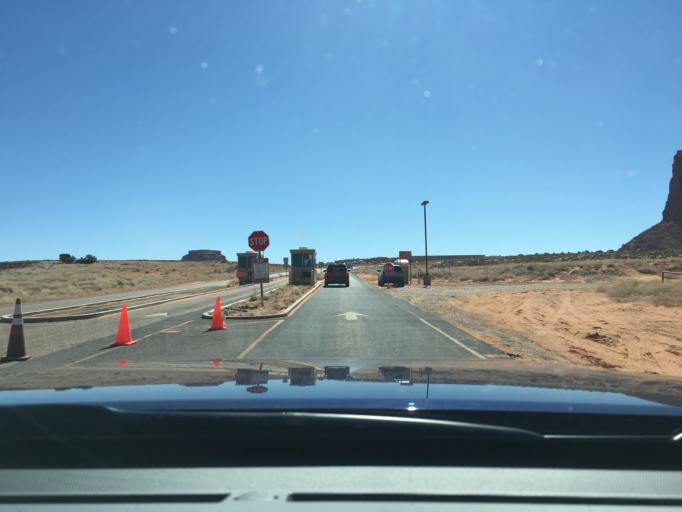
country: US
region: Arizona
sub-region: Navajo County
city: Kayenta
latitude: 36.9856
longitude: -110.1203
